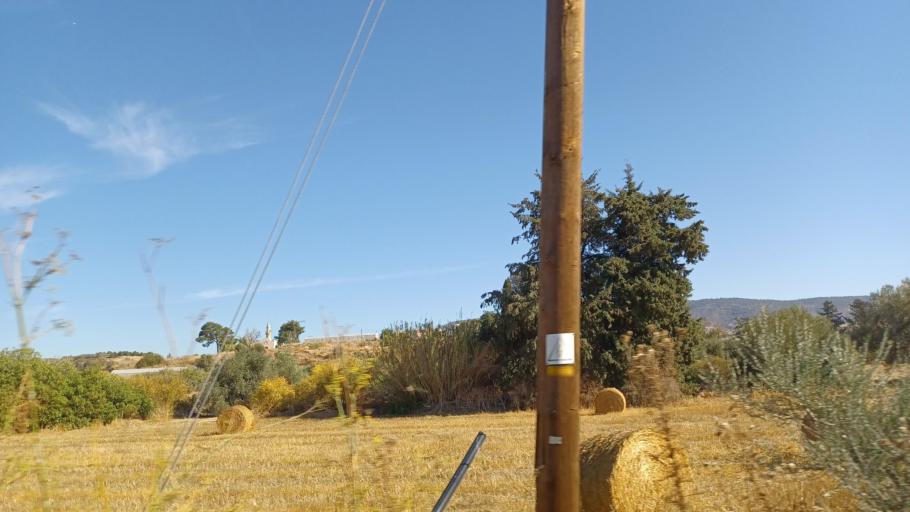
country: CY
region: Pafos
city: Polis
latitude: 35.0027
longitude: 32.4349
